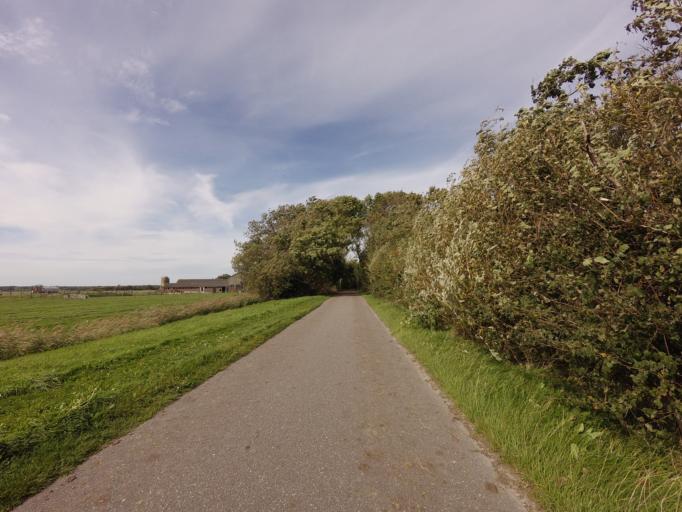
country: NL
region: North Holland
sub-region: Gemeente Texel
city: Den Burg
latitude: 53.0785
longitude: 4.7852
